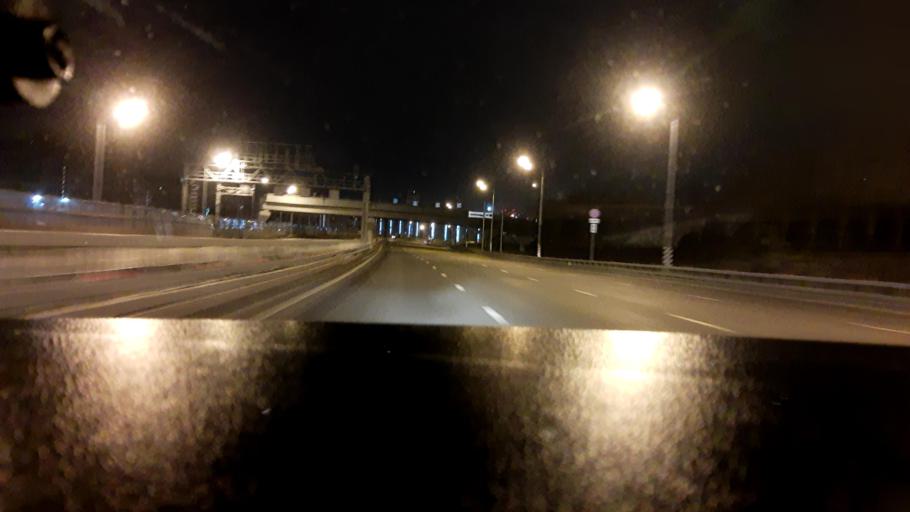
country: RU
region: Moskovskaya
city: Kastanayevo
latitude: 55.7171
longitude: 37.4947
